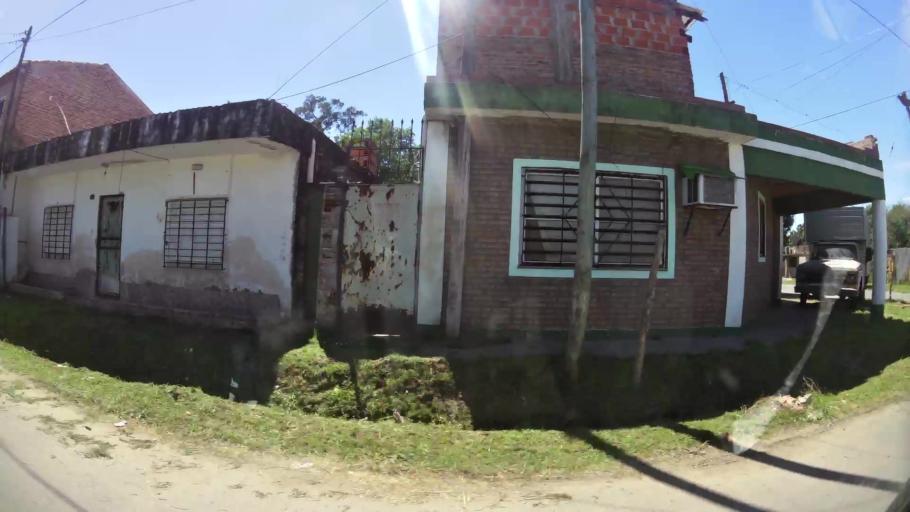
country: AR
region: Santa Fe
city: Perez
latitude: -32.9569
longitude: -60.7152
